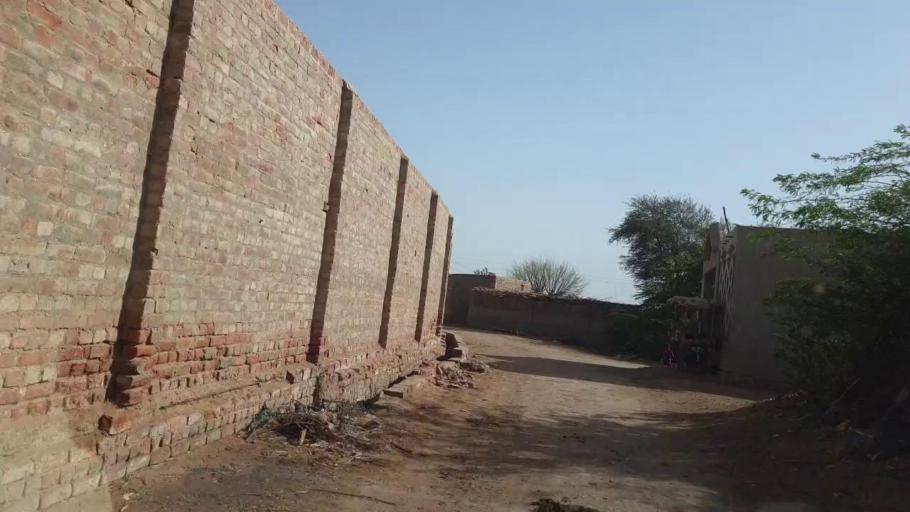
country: PK
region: Sindh
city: Tando Ghulam Ali
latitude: 25.0707
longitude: 68.8611
